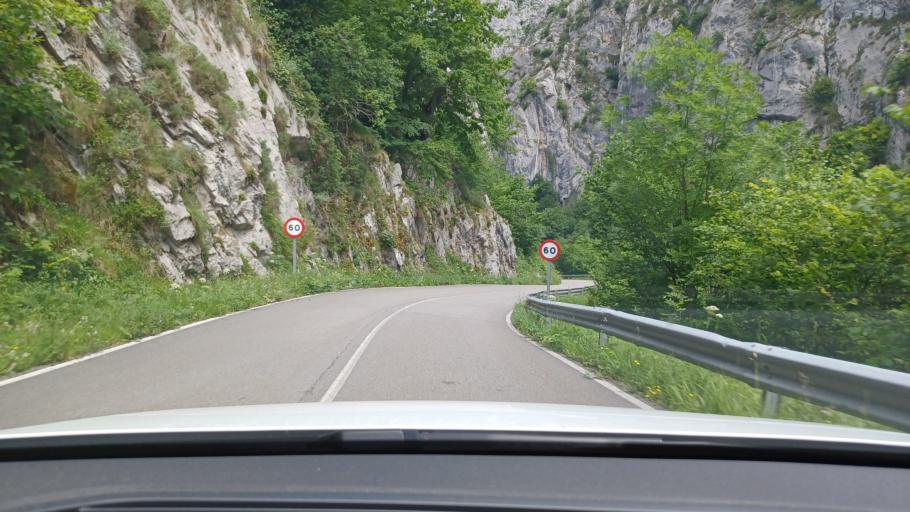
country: ES
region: Asturias
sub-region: Province of Asturias
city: La Plaza
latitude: 43.1154
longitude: -6.0500
